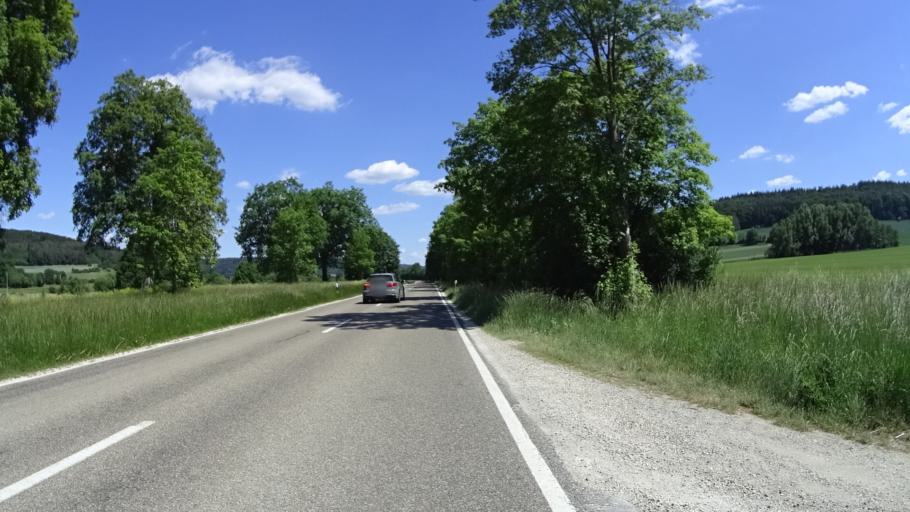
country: DE
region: Bavaria
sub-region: Regierungsbezirk Mittelfranken
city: Thalmassing
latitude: 49.0780
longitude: 11.2644
